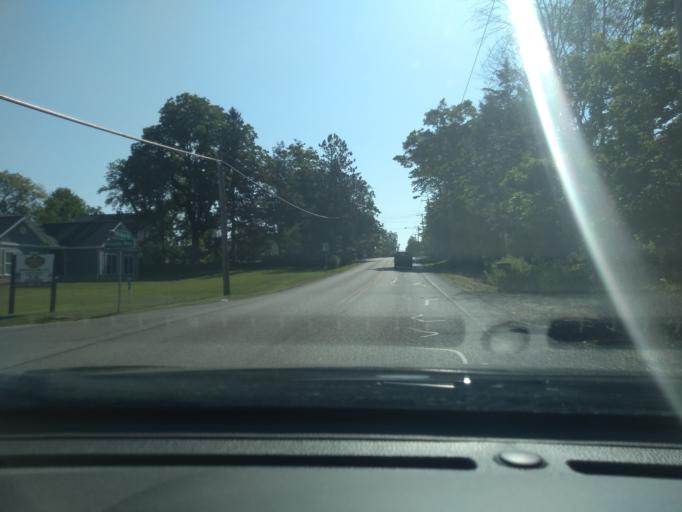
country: US
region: New York
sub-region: Erie County
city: Orchard Park
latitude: 42.7894
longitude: -78.7065
